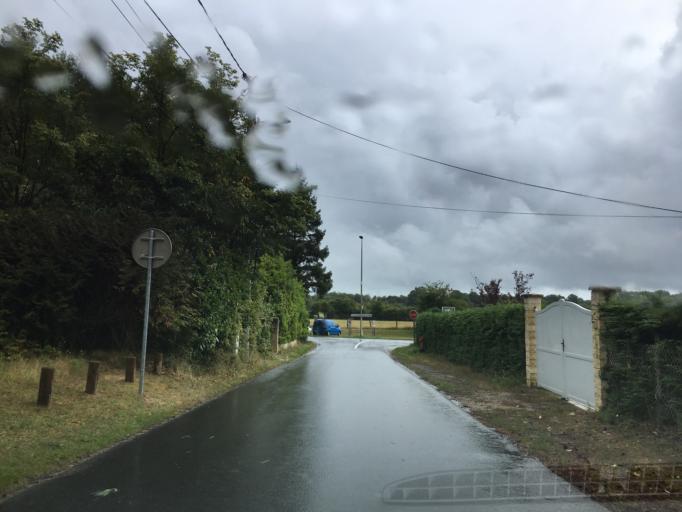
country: FR
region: Lower Normandy
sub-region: Departement du Calvados
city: Merville-Franceville-Plage
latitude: 49.2746
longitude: -0.2144
